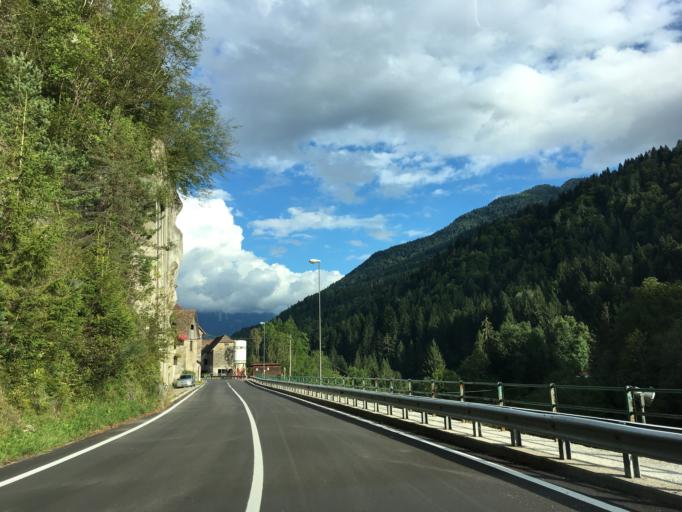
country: IT
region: Friuli Venezia Giulia
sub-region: Provincia di Udine
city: Pieria-Prato Carnico
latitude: 46.5199
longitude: 12.7932
